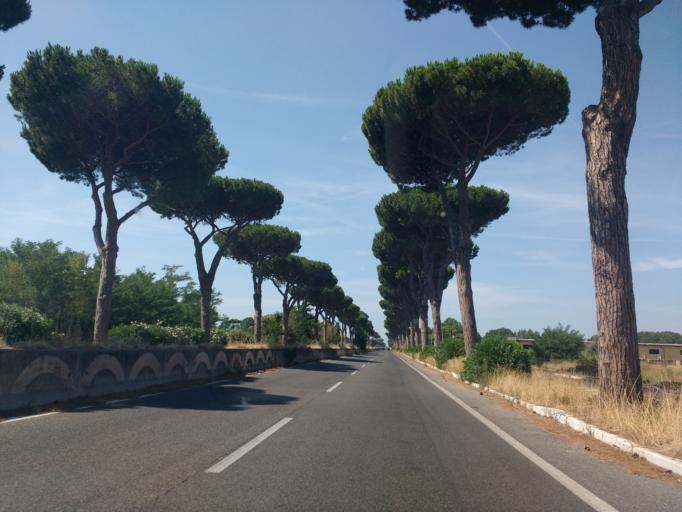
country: IT
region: Latium
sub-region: Citta metropolitana di Roma Capitale
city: Acilia-Castel Fusano-Ostia Antica
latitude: 41.7336
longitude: 12.3419
